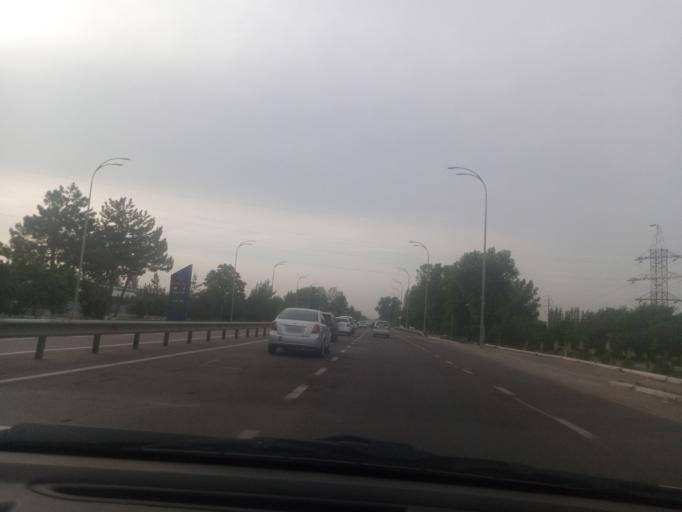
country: UZ
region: Toshkent Shahri
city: Bektemir
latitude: 41.2547
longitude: 69.3832
